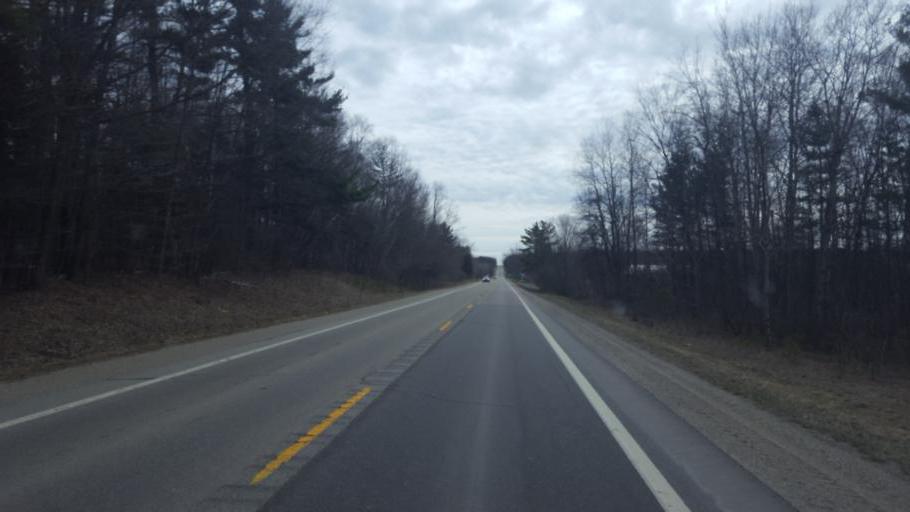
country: US
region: Michigan
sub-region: Isabella County
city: Lake Isabella
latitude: 43.6943
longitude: -85.1467
